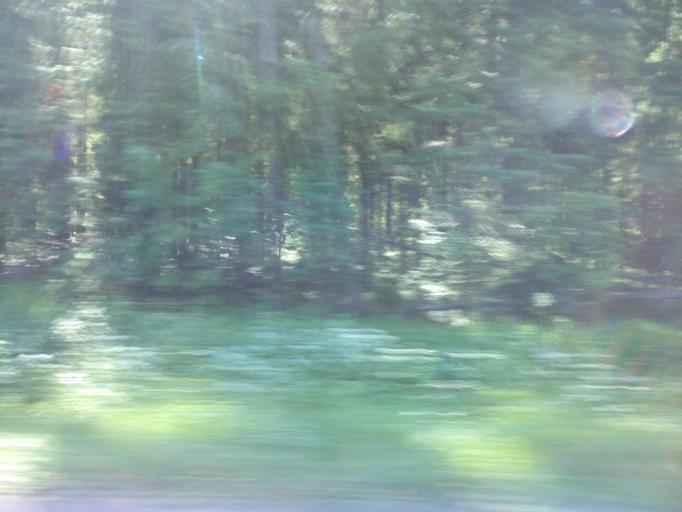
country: FI
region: Southern Savonia
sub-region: Savonlinna
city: Savonlinna
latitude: 61.8776
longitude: 28.9637
